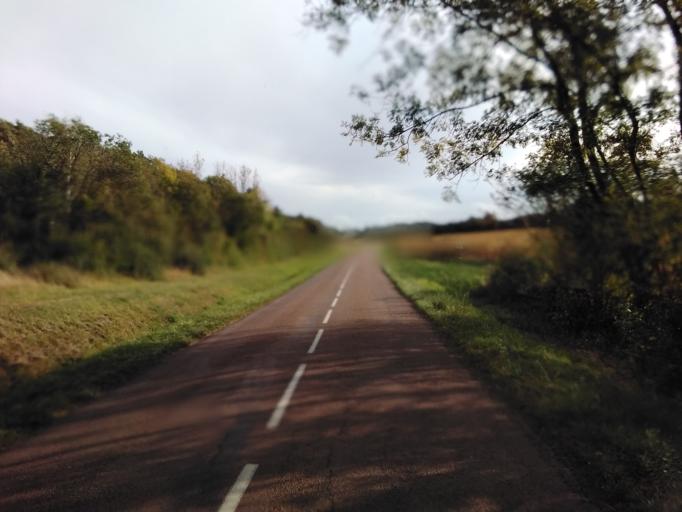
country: FR
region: Champagne-Ardenne
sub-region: Departement de l'Aube
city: Les Riceys
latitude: 47.8800
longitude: 4.3531
